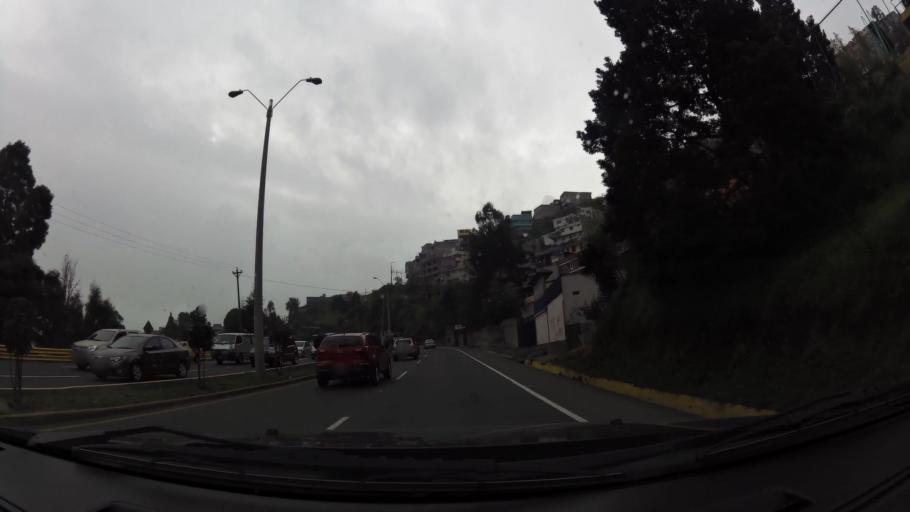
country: EC
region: Pichincha
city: Quito
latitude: -0.2273
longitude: -78.4922
